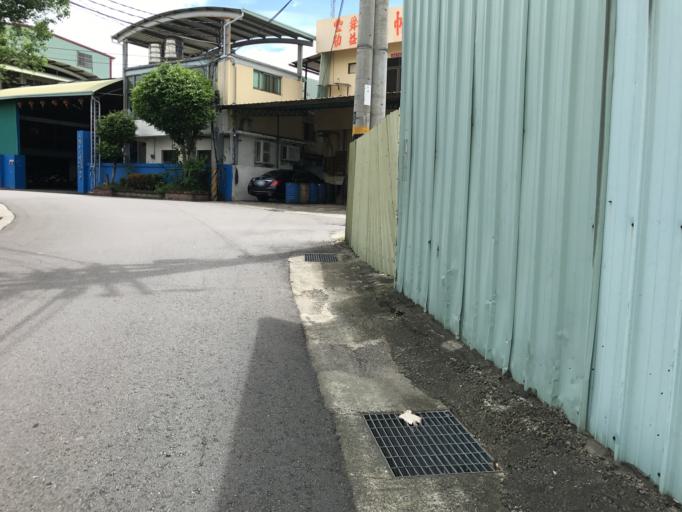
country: TW
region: Taiwan
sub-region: Taichung City
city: Taichung
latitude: 24.0797
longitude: 120.7132
